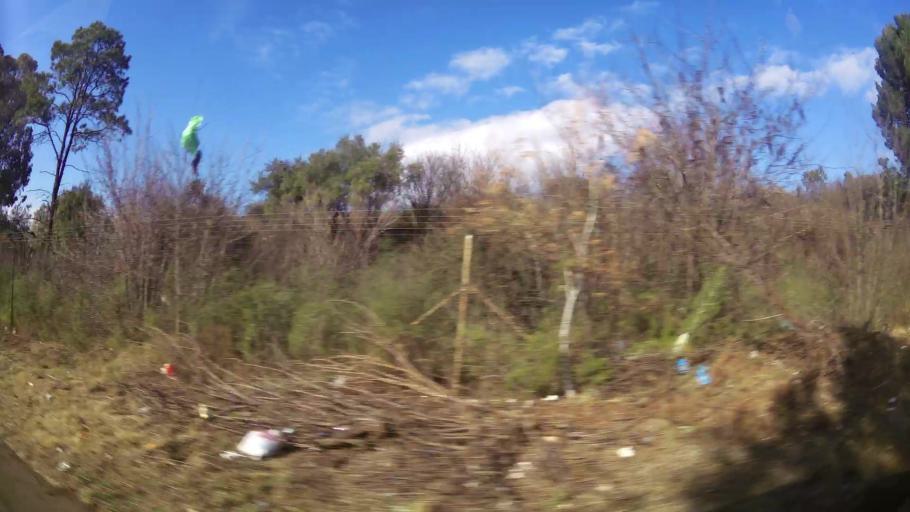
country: ZA
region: Gauteng
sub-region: Sedibeng District Municipality
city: Meyerton
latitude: -26.5051
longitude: 28.0621
